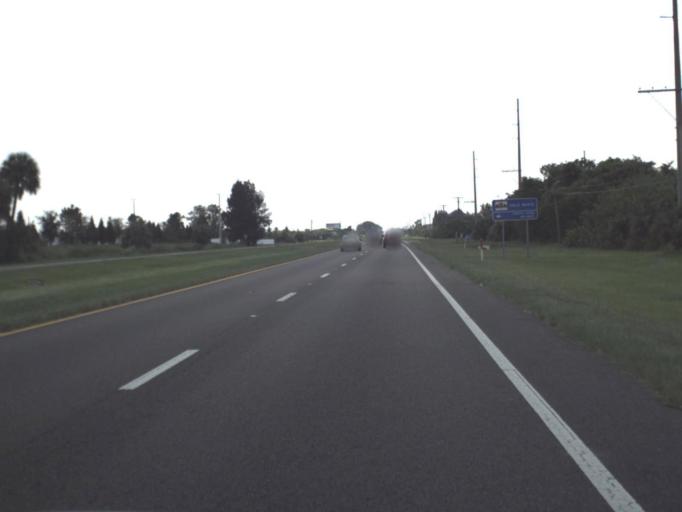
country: US
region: Florida
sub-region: Hillsborough County
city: Apollo Beach
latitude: 27.8024
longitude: -82.3844
